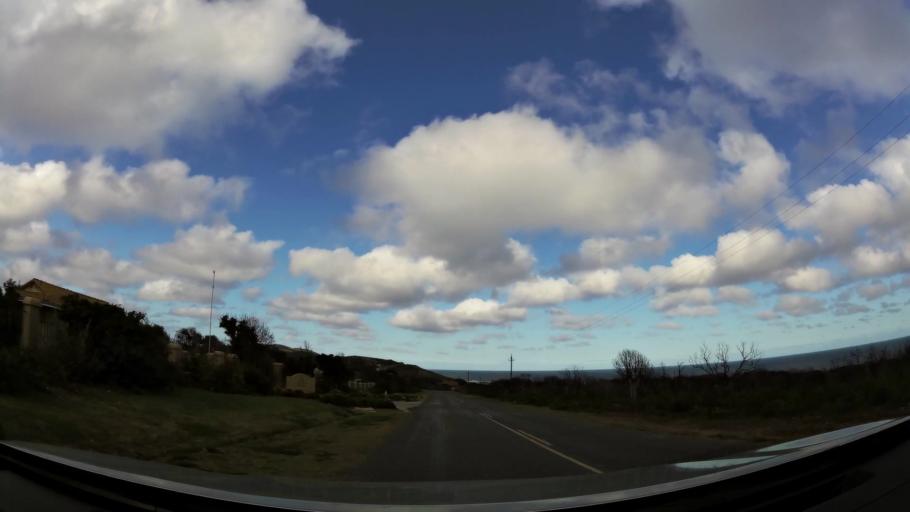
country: ZA
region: Western Cape
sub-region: Eden District Municipality
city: Plettenberg Bay
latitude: -34.0972
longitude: 23.3678
